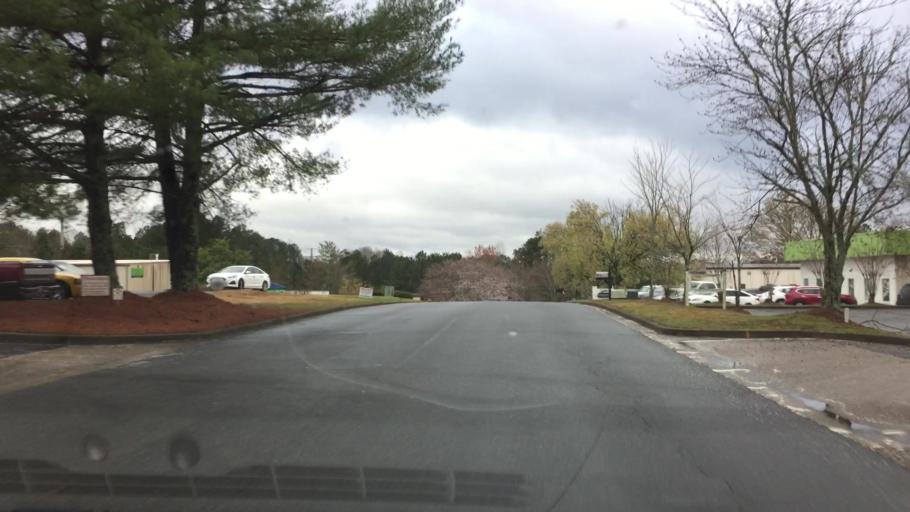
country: US
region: Georgia
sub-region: Fulton County
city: Milton
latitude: 34.1359
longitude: -84.2538
